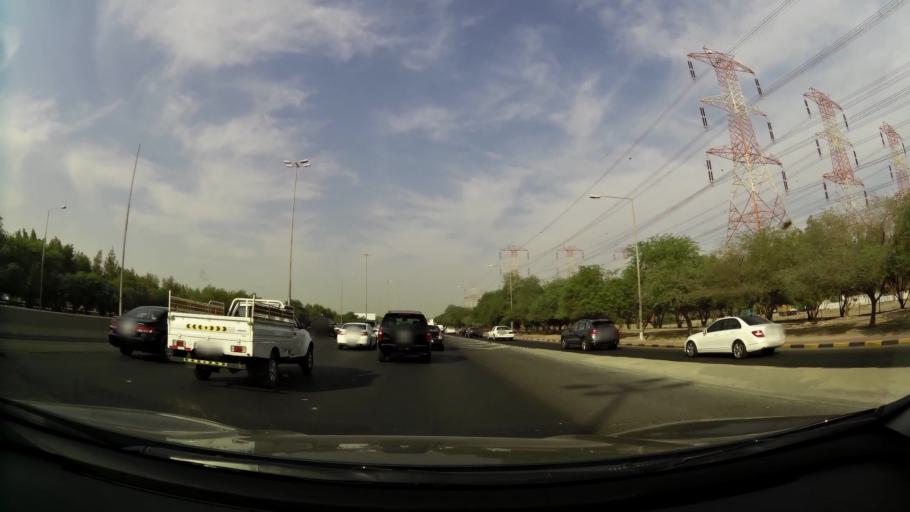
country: KW
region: Mubarak al Kabir
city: Sabah as Salim
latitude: 29.2645
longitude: 48.0547
